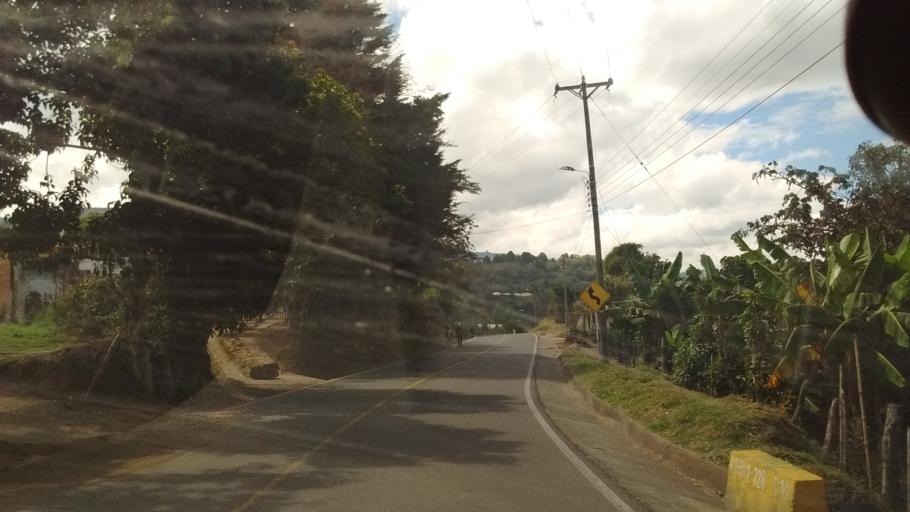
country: CO
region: Cauca
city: Cajibio
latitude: 2.6289
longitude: -76.5192
